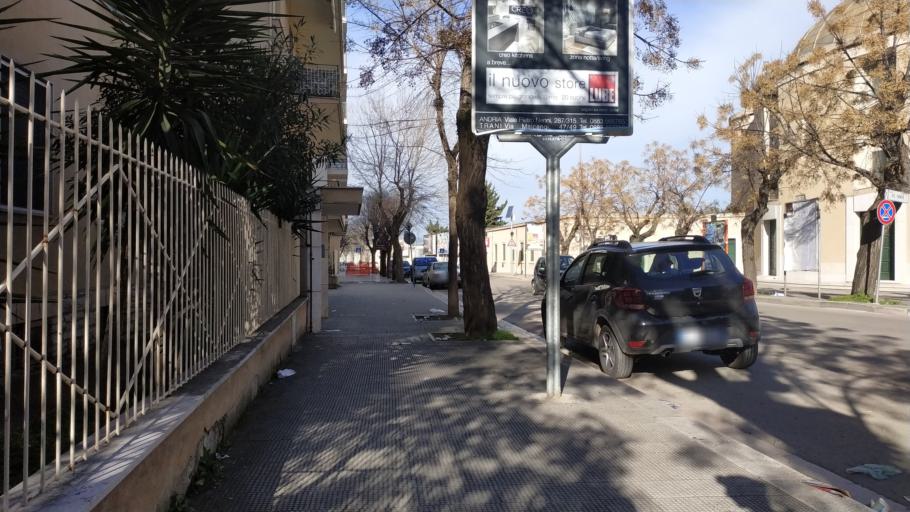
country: IT
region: Apulia
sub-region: Provincia di Barletta - Andria - Trani
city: Andria
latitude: 41.2355
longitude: 16.3081
